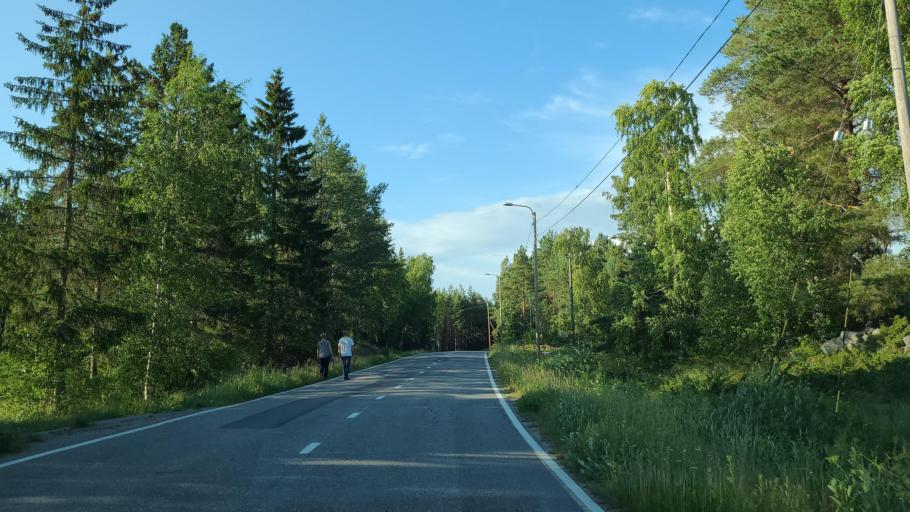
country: FI
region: Ostrobothnia
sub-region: Vaasa
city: Replot
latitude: 63.3507
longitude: 21.3001
